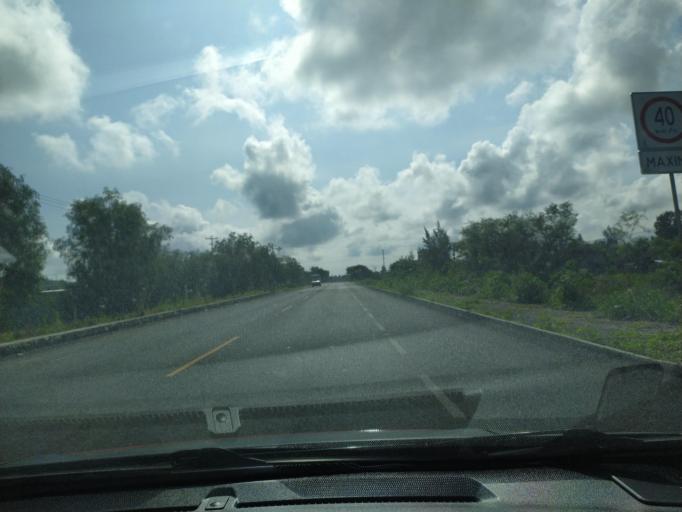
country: MX
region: Guanajuato
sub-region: San Francisco del Rincon
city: San Ignacio de Hidalgo
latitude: 20.8917
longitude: -101.9506
